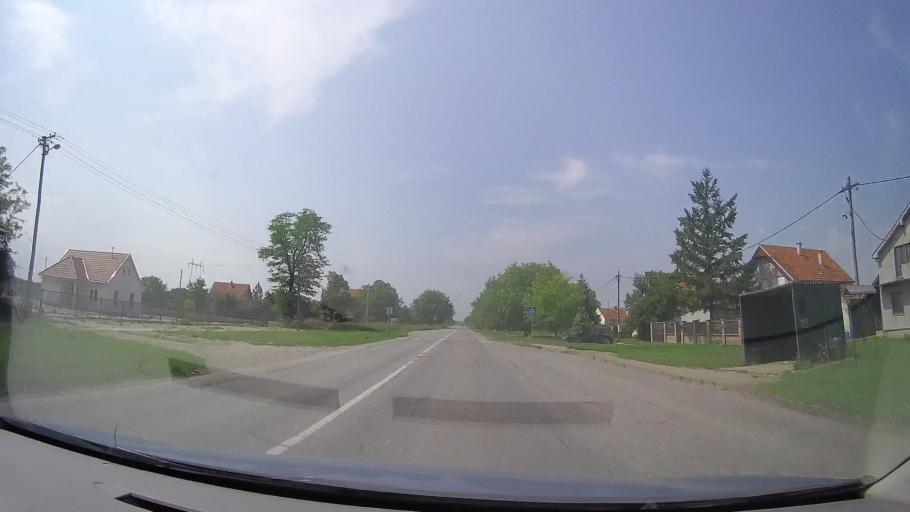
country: RS
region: Autonomna Pokrajina Vojvodina
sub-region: Juznobanatski Okrug
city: Pancevo
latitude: 44.9254
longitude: 20.6618
